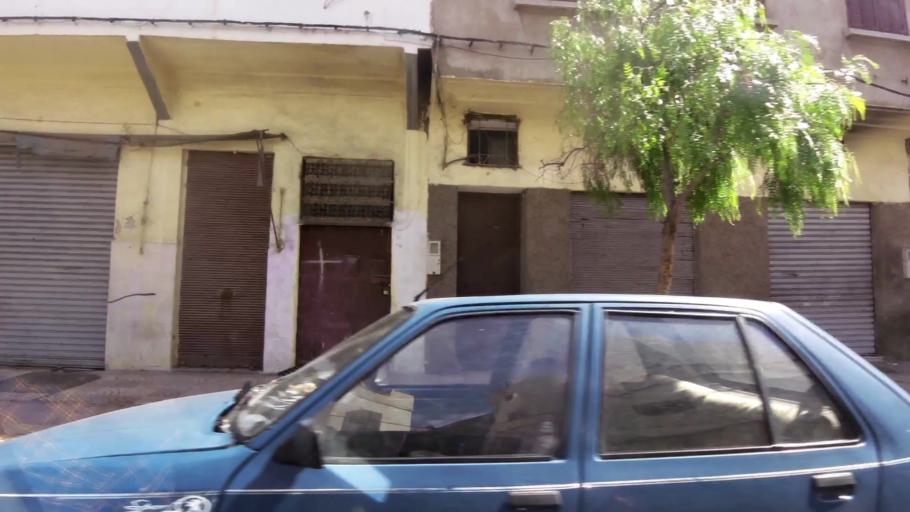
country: MA
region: Grand Casablanca
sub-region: Casablanca
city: Casablanca
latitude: 33.6057
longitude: -7.6280
